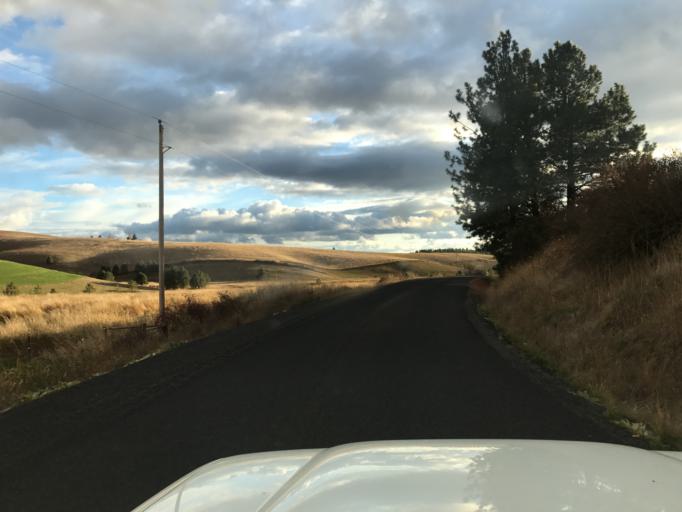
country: US
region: Idaho
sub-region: Latah County
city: Moscow
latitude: 46.7944
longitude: -116.9607
